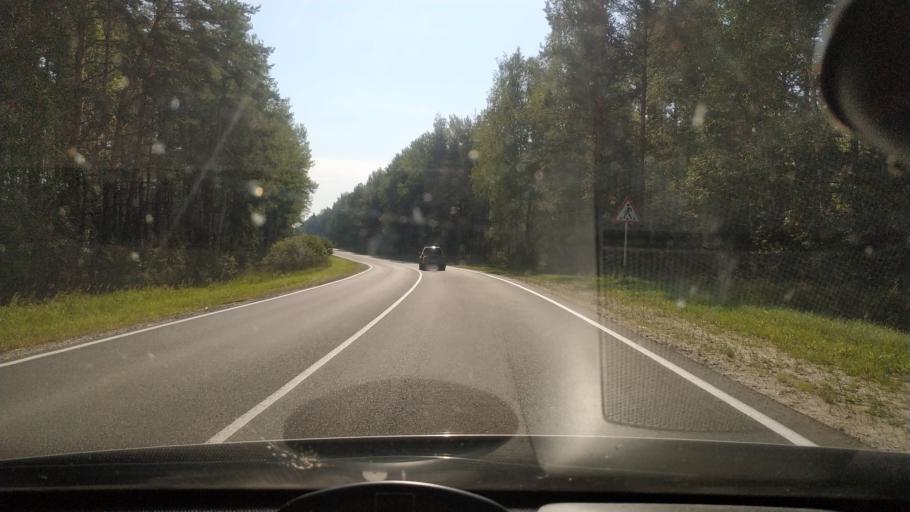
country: RU
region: Rjazan
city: Spas-Klepiki
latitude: 55.2253
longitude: 40.0653
